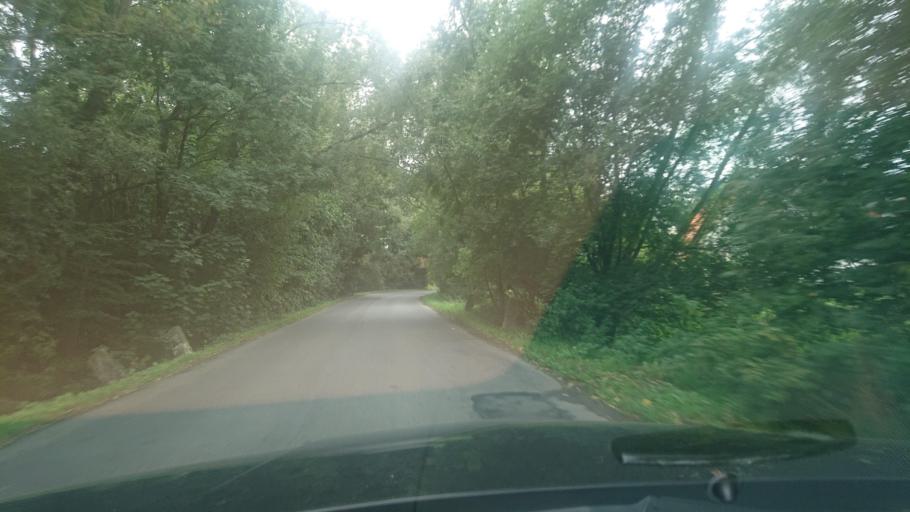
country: PL
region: Lower Silesian Voivodeship
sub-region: Powiat klodzki
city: Miedzylesie
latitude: 50.2158
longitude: 16.6889
